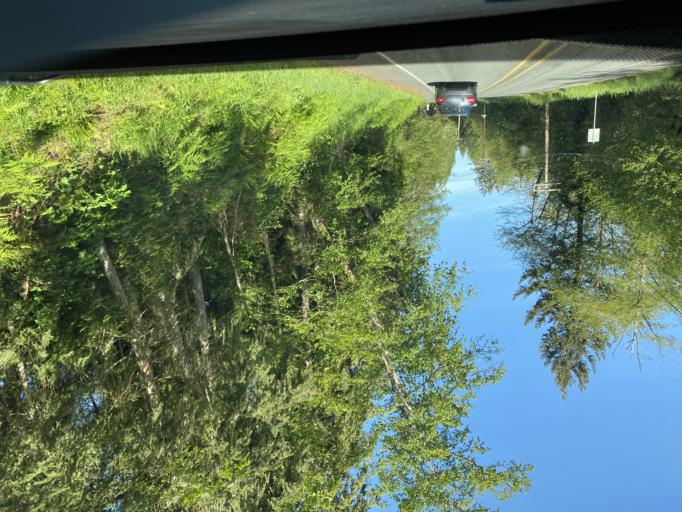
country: US
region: Washington
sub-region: Island County
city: Langley
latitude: 48.0366
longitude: -122.4220
